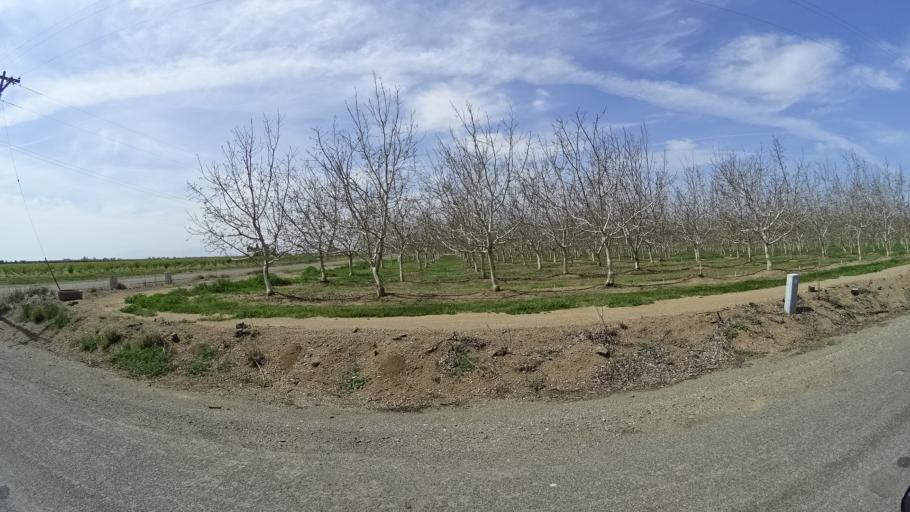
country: US
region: California
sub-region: Glenn County
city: Orland
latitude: 39.7872
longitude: -122.1598
